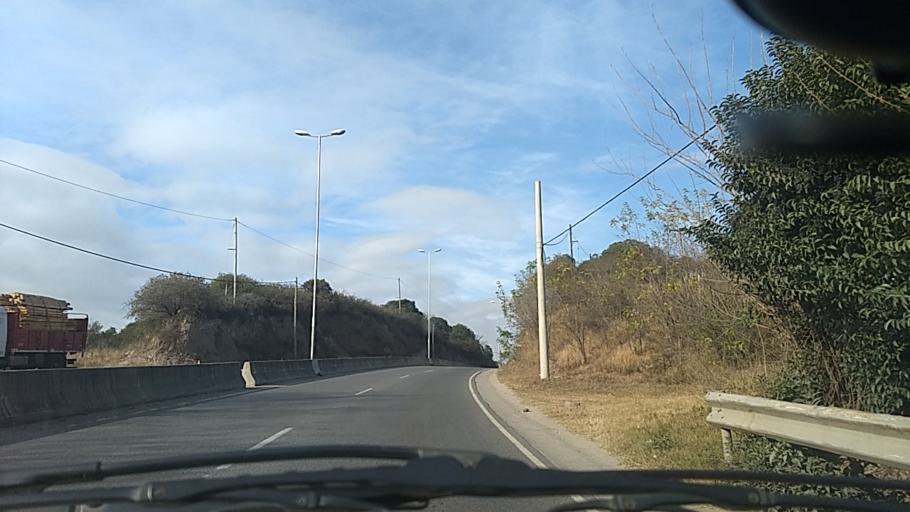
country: AR
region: Cordoba
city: Salsipuedes
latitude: -31.1459
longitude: -64.2980
